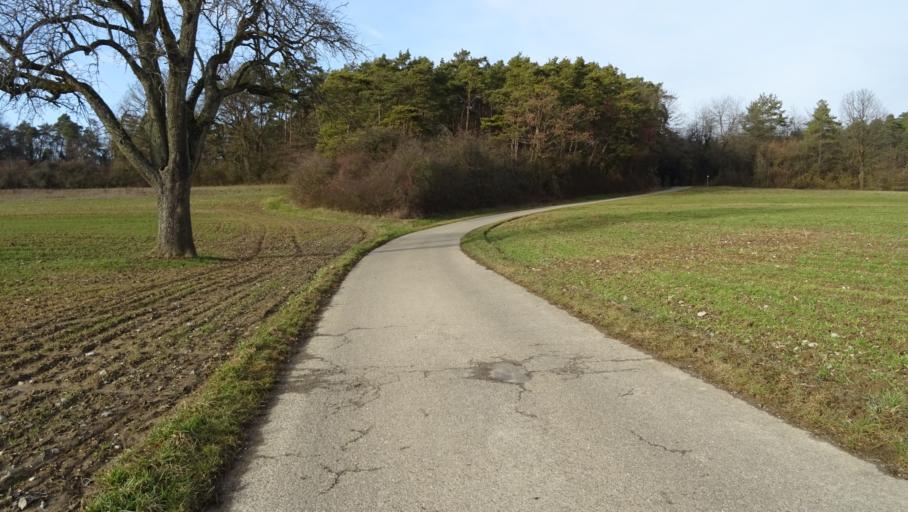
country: DE
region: Baden-Wuerttemberg
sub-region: Karlsruhe Region
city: Mosbach
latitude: 49.3664
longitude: 9.1871
